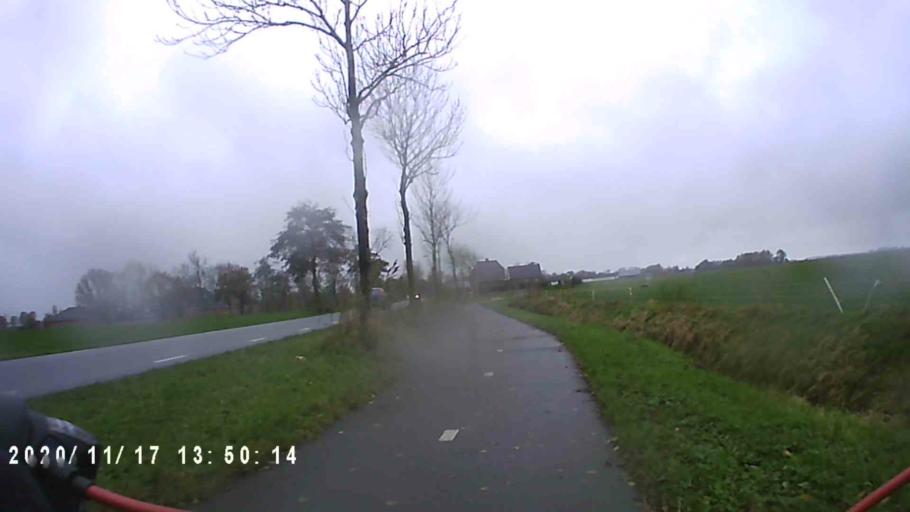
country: NL
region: Groningen
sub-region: Gemeente Zuidhorn
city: Zuidhorn
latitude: 53.2305
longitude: 6.3676
